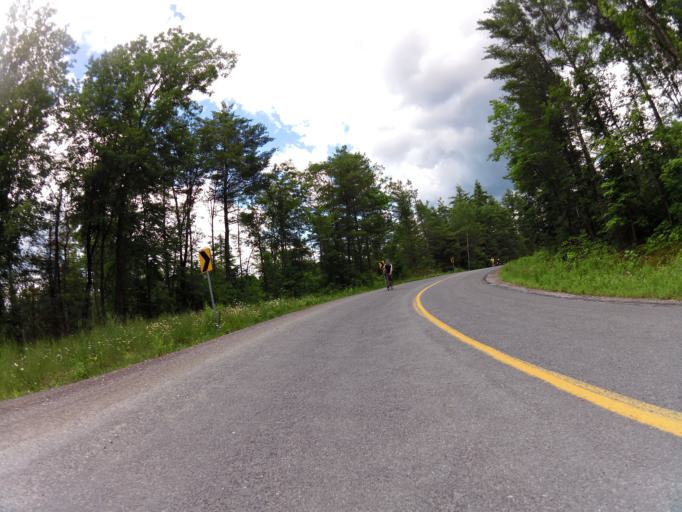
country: CA
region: Ontario
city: Renfrew
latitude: 45.0480
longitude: -76.6949
